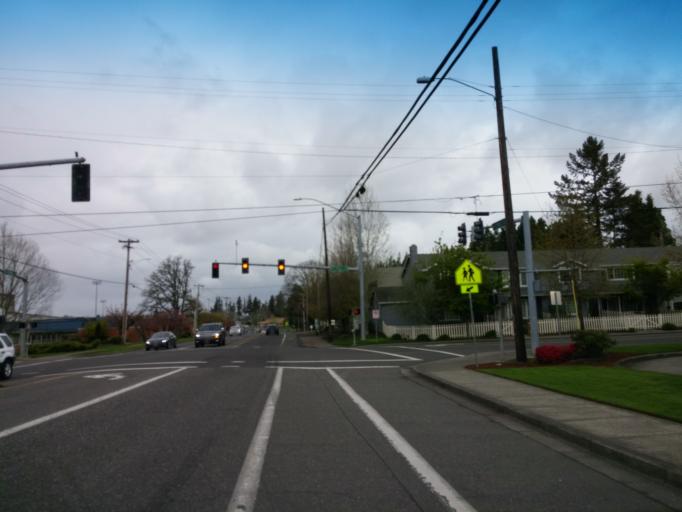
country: US
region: Oregon
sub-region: Washington County
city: Cedar Mill
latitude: 45.5282
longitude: -122.8175
